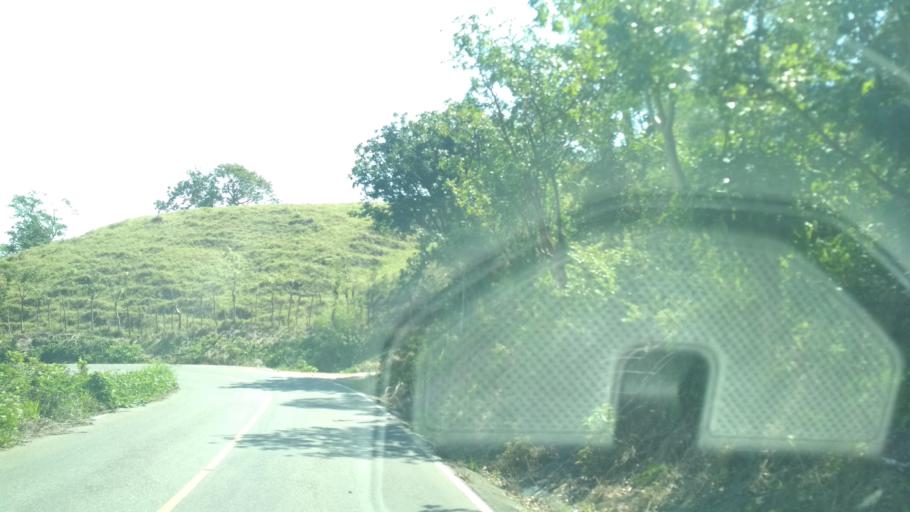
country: MX
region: Veracruz
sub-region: Papantla
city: Polutla
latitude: 20.4668
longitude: -97.2229
